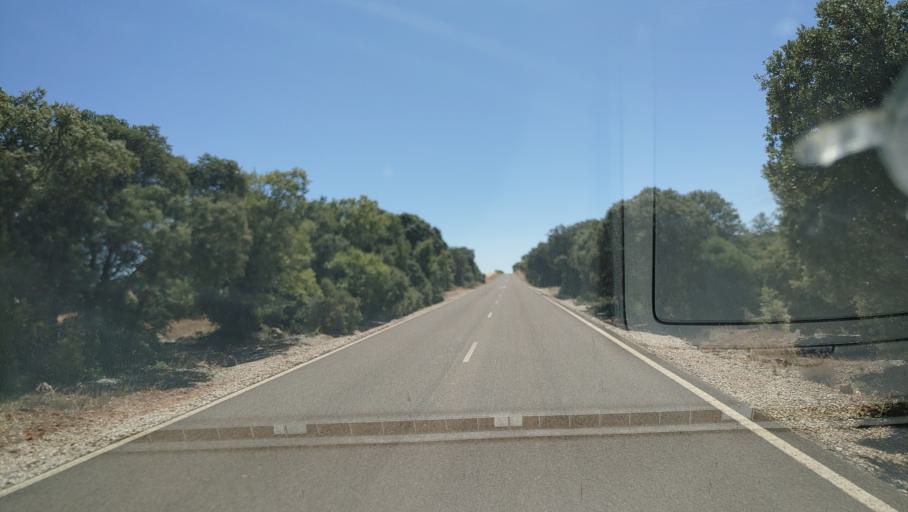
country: ES
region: Castille-La Mancha
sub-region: Provincia de Ciudad Real
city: Villahermosa
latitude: 38.8155
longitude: -2.8334
